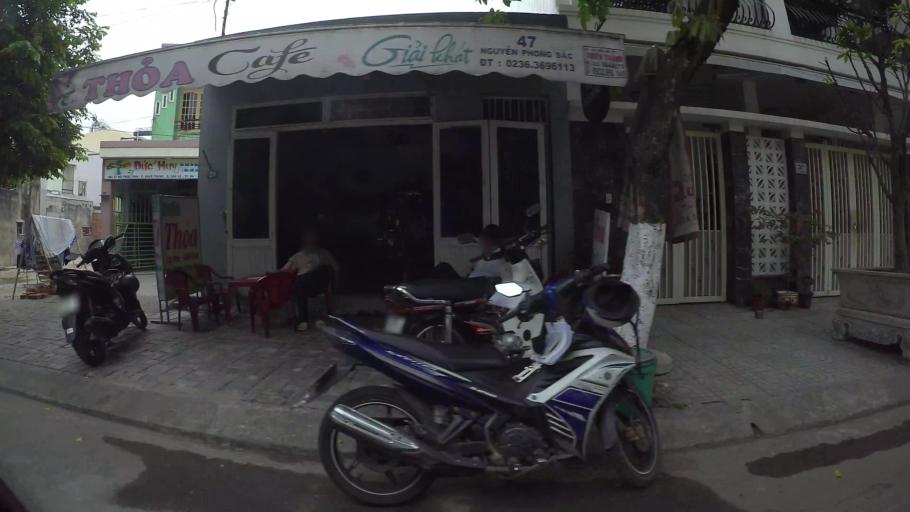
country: VN
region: Da Nang
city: Cam Le
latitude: 16.0276
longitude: 108.2096
